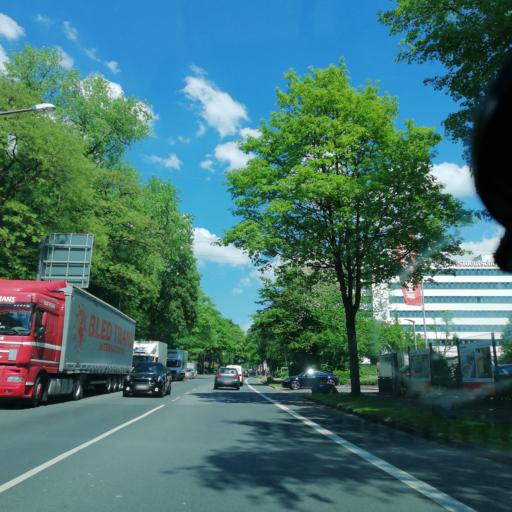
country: DE
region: North Rhine-Westphalia
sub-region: Regierungsbezirk Dusseldorf
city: Wuppertal
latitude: 51.2546
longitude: 7.1053
